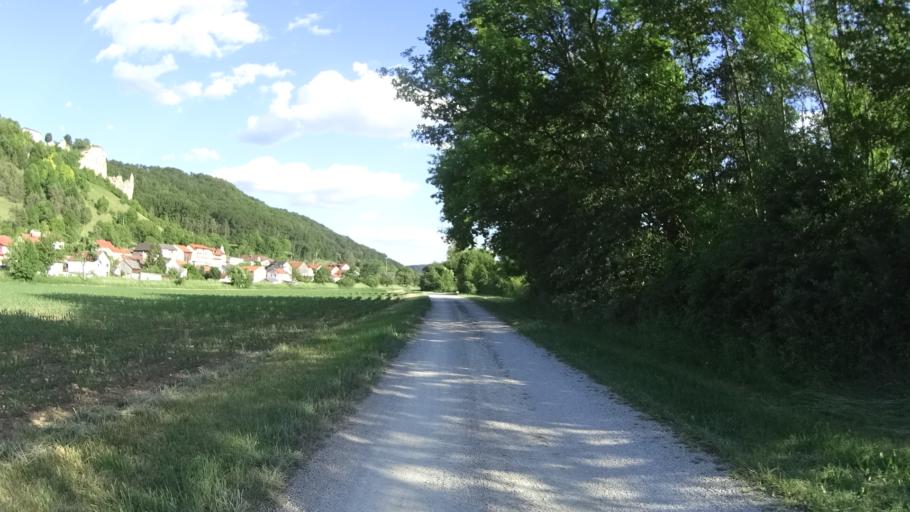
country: DE
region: Bavaria
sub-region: Upper Palatinate
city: Dietfurt
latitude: 48.9996
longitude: 11.6299
